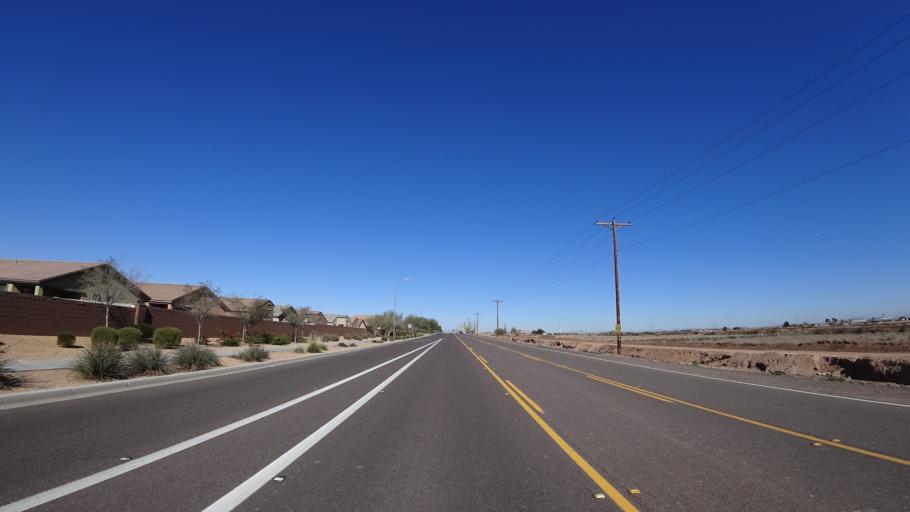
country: US
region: Arizona
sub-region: Maricopa County
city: Tolleson
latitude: 33.4003
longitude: -112.2722
